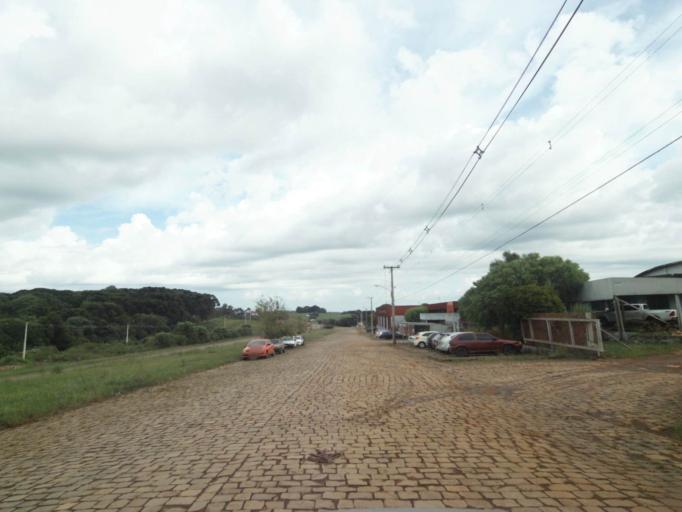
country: BR
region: Rio Grande do Sul
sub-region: Lagoa Vermelha
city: Lagoa Vermelha
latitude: -28.2376
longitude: -51.5001
